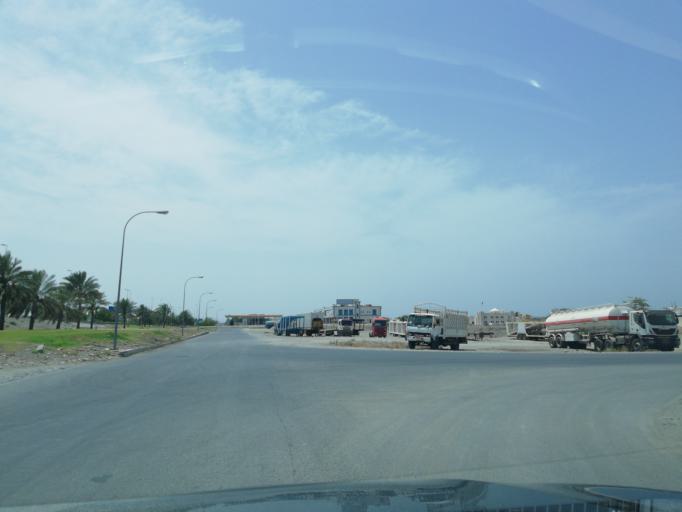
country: OM
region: Muhafazat Masqat
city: As Sib al Jadidah
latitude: 23.6565
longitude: 58.2022
